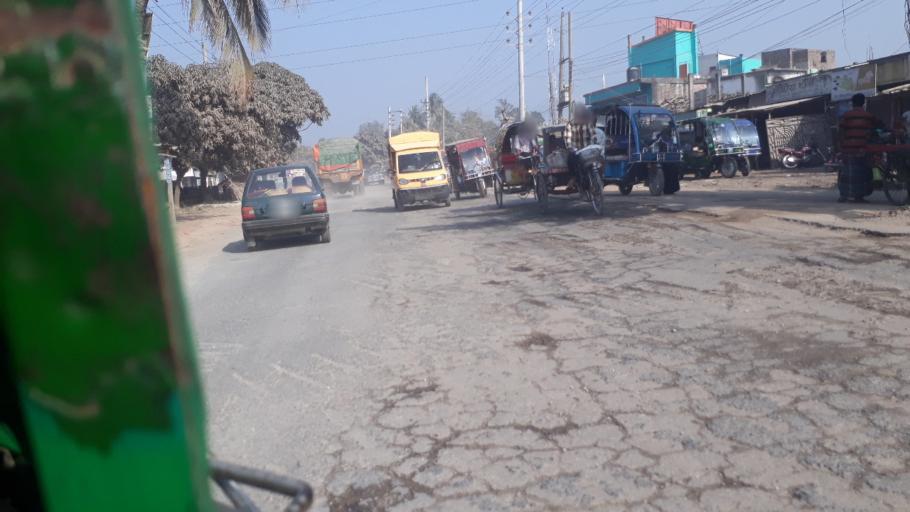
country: BD
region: Khulna
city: Kushtia
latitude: 23.8862
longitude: 89.1059
